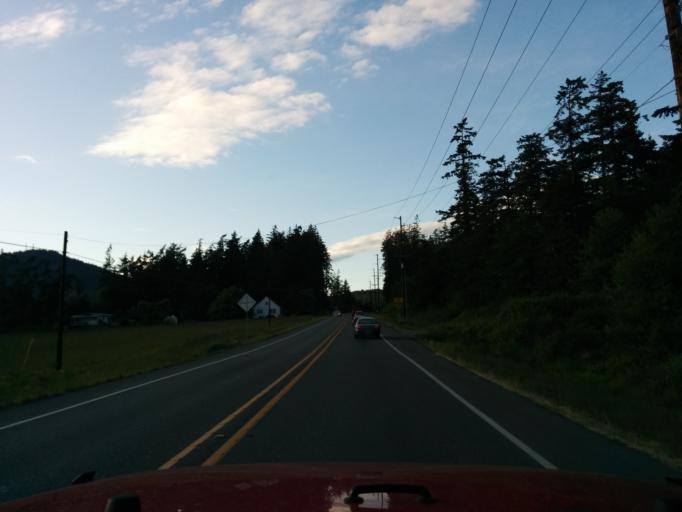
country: US
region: Washington
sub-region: Skagit County
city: Anacortes
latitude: 48.4316
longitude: -122.6075
